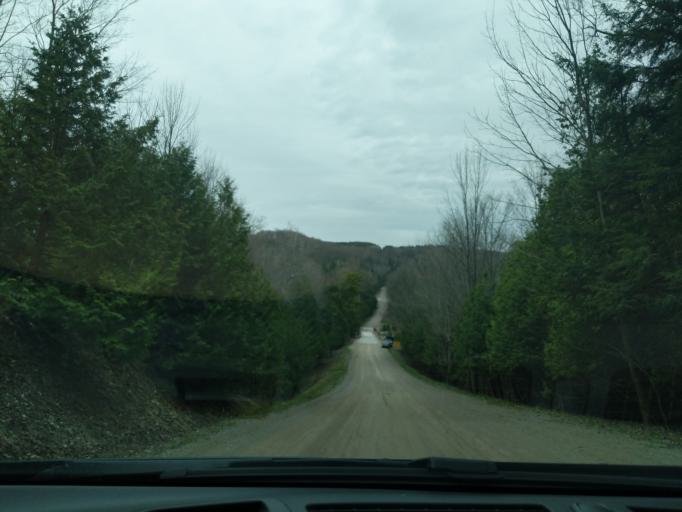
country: CA
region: Ontario
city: Orangeville
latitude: 43.9982
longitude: -80.0153
